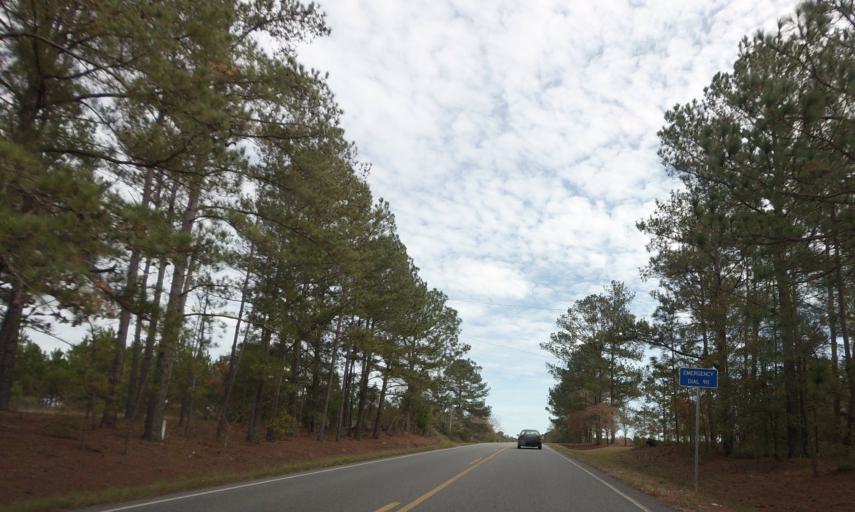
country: US
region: Georgia
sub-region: Dodge County
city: Chester
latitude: 32.4102
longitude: -83.2127
